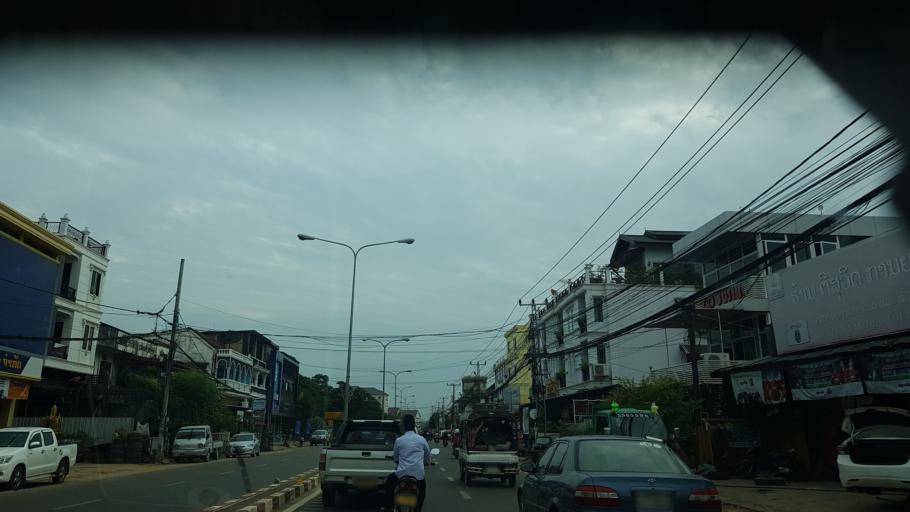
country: LA
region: Vientiane
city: Vientiane
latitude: 17.9524
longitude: 102.6188
